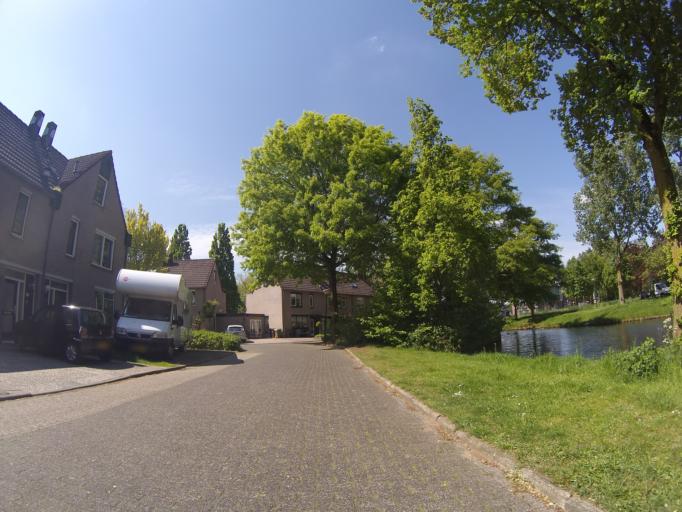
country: NL
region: Utrecht
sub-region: Gemeente Soest
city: Soest
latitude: 52.1730
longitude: 5.2789
